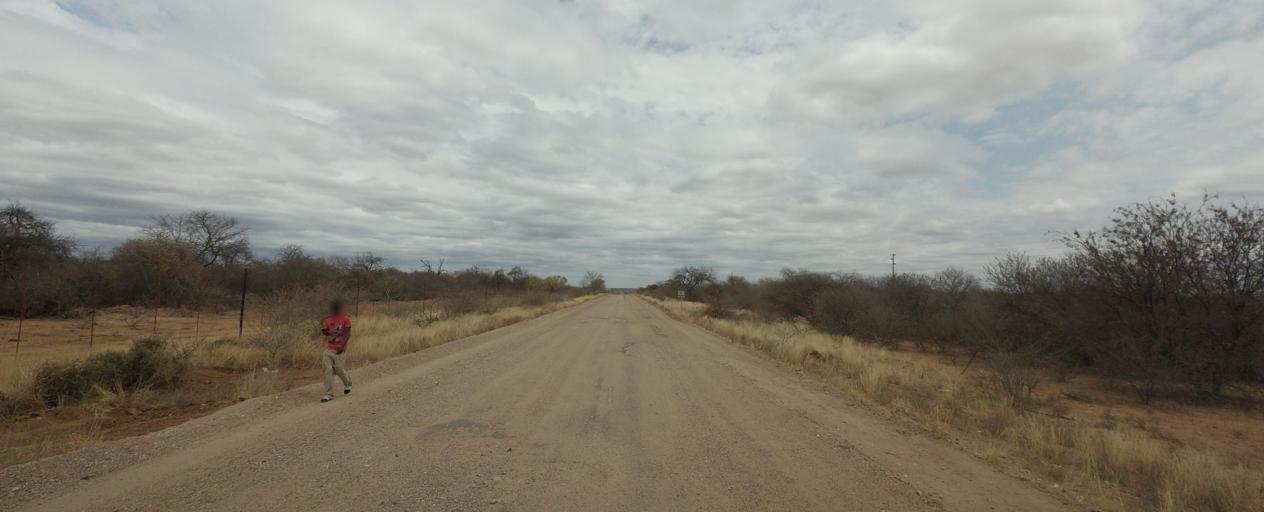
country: BW
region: Central
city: Mathathane
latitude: -22.6796
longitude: 28.6624
